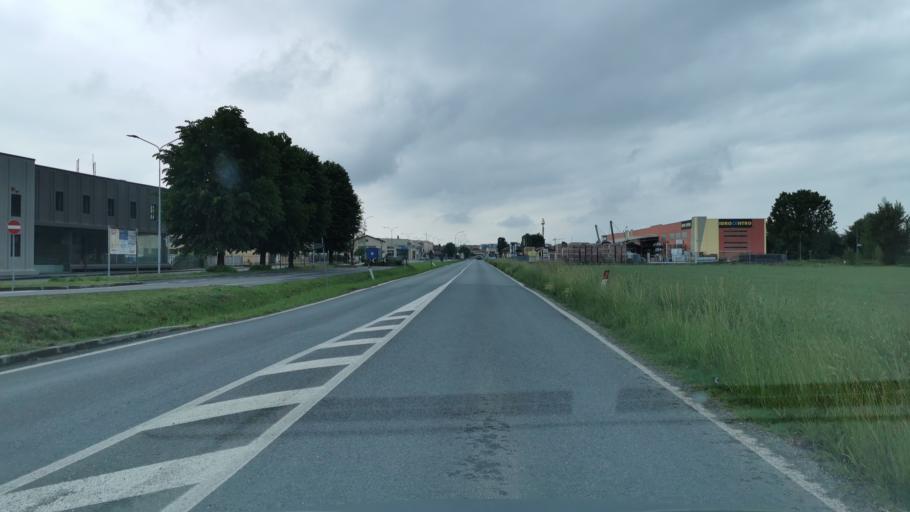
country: IT
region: Piedmont
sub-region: Provincia di Cuneo
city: Savigliano
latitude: 44.6594
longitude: 7.6562
